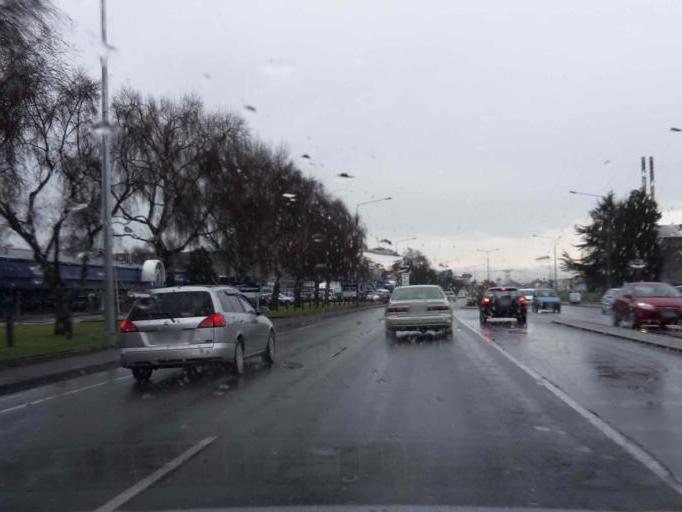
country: NZ
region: Canterbury
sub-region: Christchurch City
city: Christchurch
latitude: -43.5393
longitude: 172.5728
